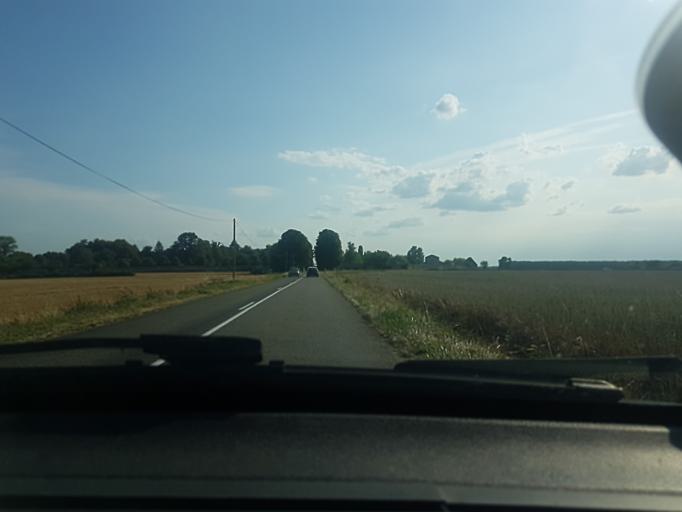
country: FR
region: Bourgogne
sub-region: Departement de Saone-et-Loire
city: Sennecey-le-Grand
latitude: 46.6757
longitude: 4.8216
